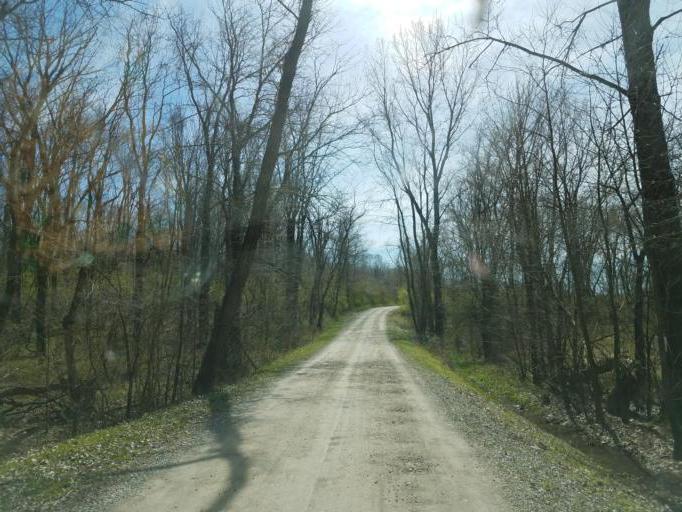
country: US
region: Ohio
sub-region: Delaware County
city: Ashley
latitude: 40.4270
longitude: -83.0593
